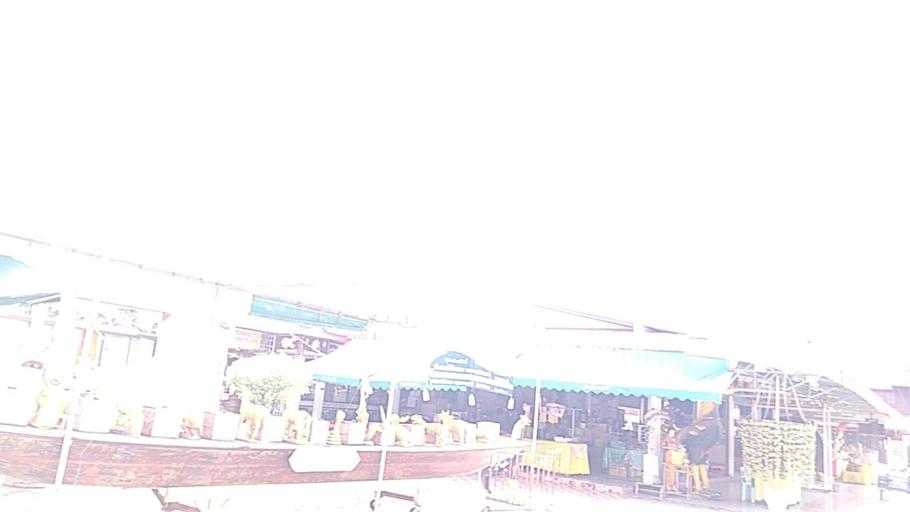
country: TH
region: Nonthaburi
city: Sai Noi
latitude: 13.9787
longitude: 100.3111
